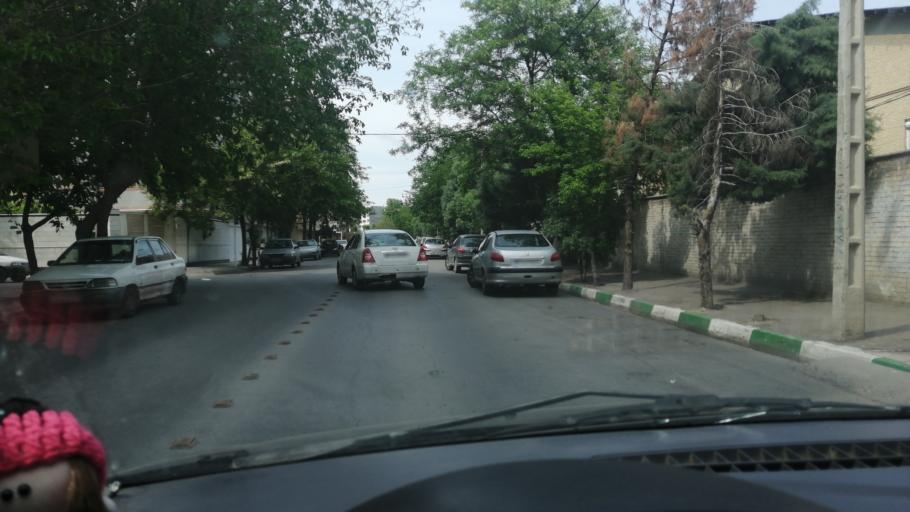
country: IR
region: Razavi Khorasan
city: Mashhad
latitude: 36.3262
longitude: 59.5670
